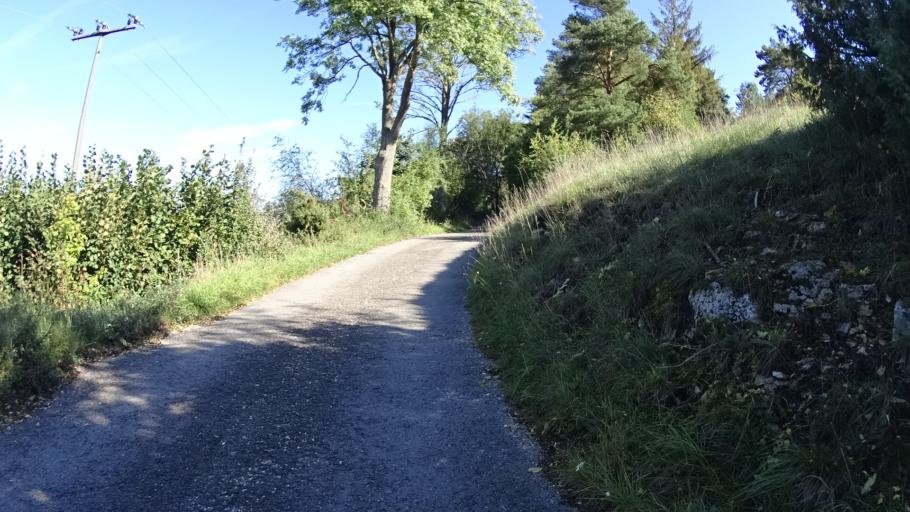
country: DE
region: Bavaria
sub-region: Upper Bavaria
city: Walting
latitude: 48.8893
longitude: 11.2678
